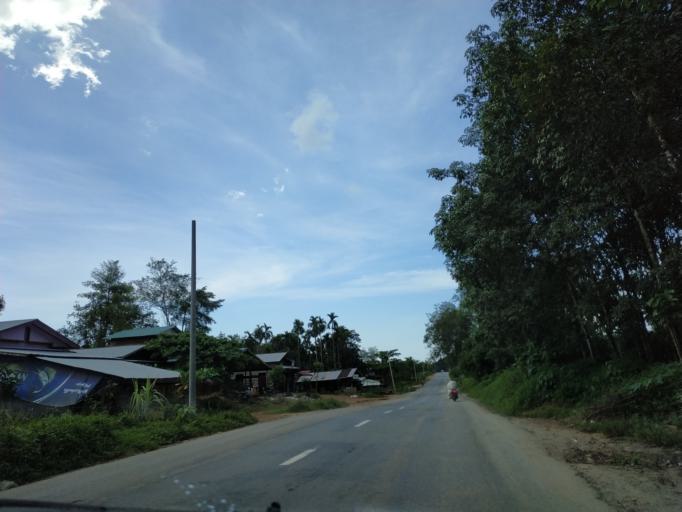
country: MM
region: Mon
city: Kyaikkami
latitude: 15.4970
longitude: 97.8707
